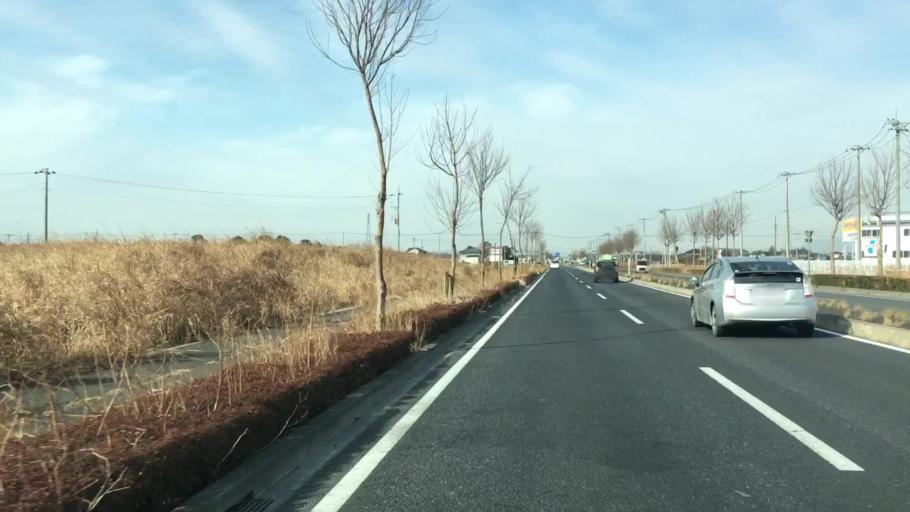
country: JP
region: Gunma
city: Tatebayashi
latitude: 36.2309
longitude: 139.4883
